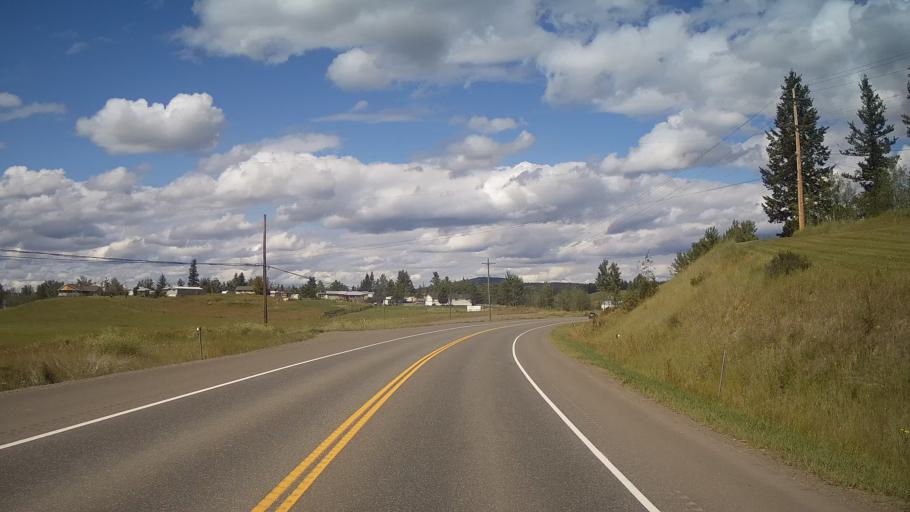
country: CA
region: British Columbia
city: Cache Creek
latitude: 51.7002
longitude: -121.3222
